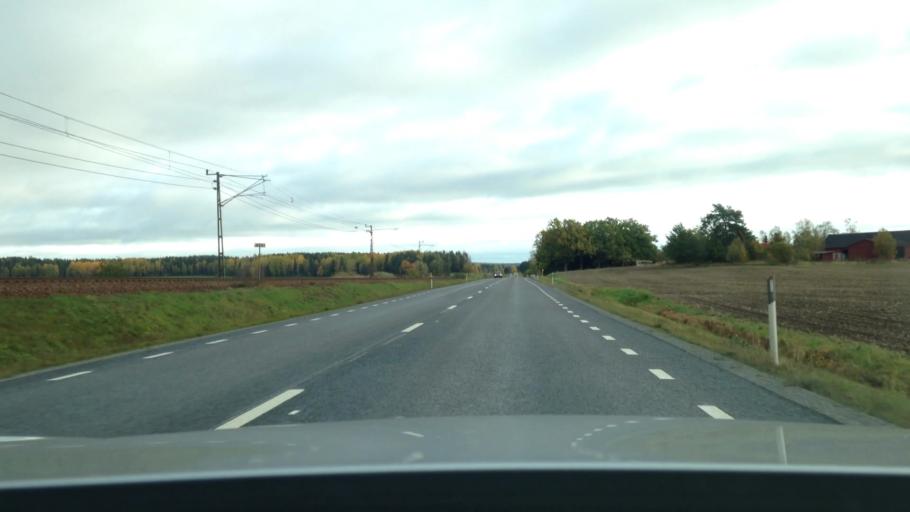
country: SE
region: Vaermland
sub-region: Saffle Kommun
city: Saeffle
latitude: 59.1585
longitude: 12.9893
